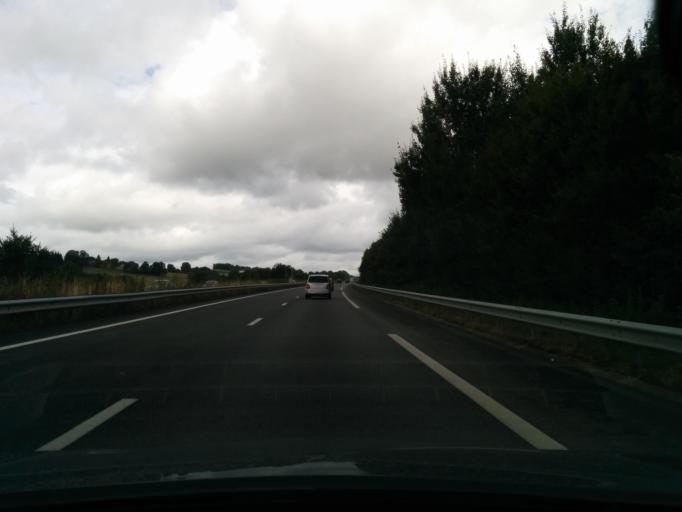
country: FR
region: Limousin
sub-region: Departement de la Correze
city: Vigeois
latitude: 45.4298
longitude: 1.5129
